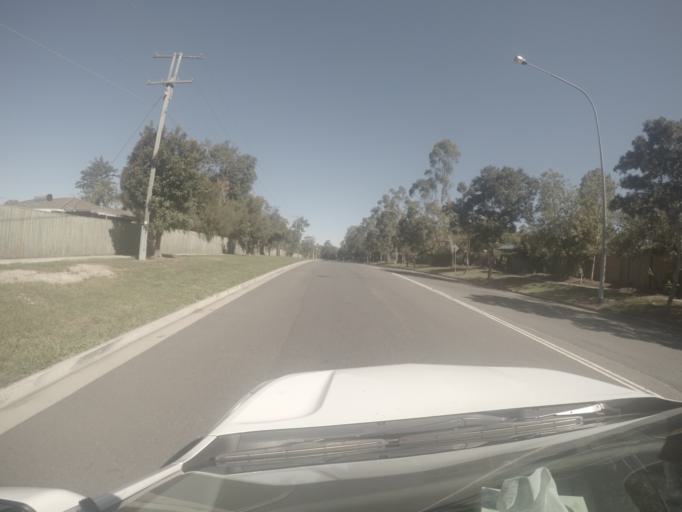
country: AU
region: Queensland
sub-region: Ipswich
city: Springfield
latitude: -27.6446
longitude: 152.9191
